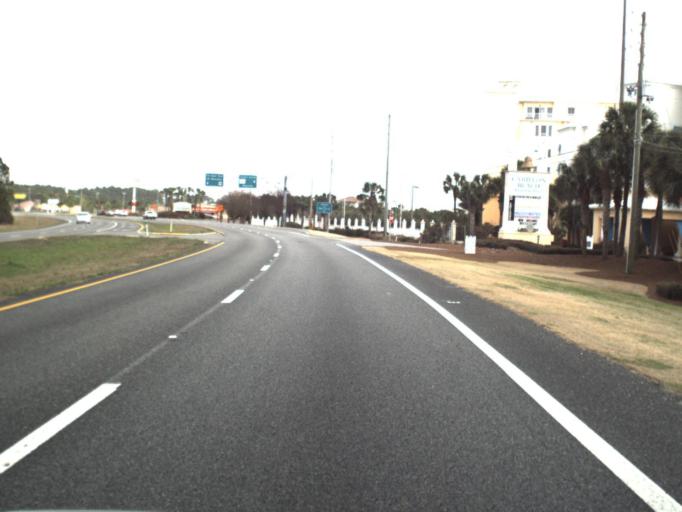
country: US
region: Florida
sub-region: Bay County
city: Laguna Beach
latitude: 30.2661
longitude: -85.9780
